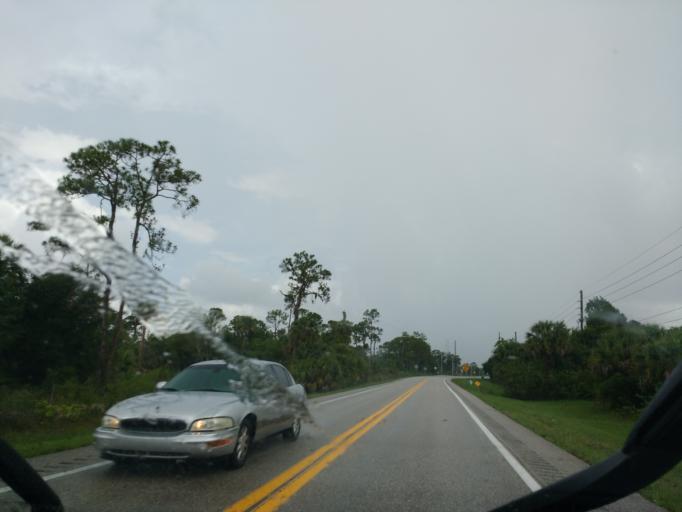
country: US
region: Florida
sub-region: Charlotte County
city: Charlotte Park
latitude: 26.8561
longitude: -82.0227
